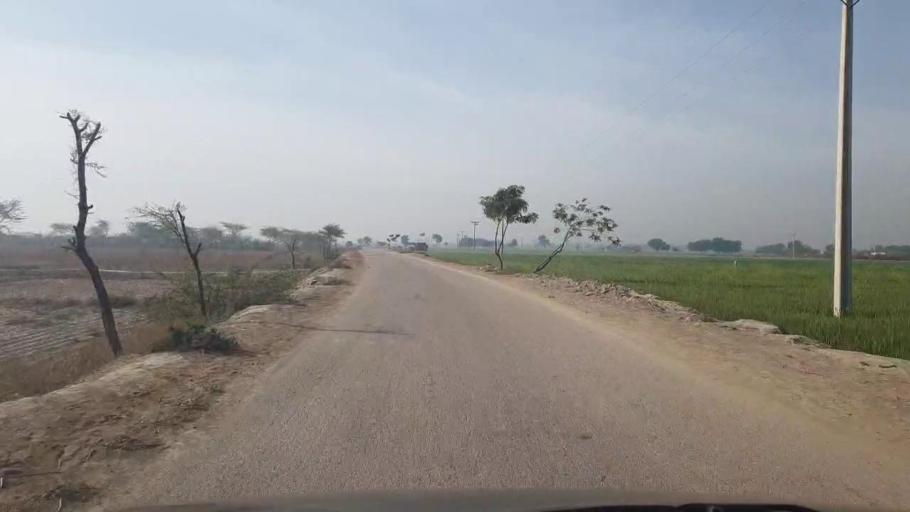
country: PK
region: Sindh
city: Umarkot
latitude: 25.3512
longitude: 69.6981
